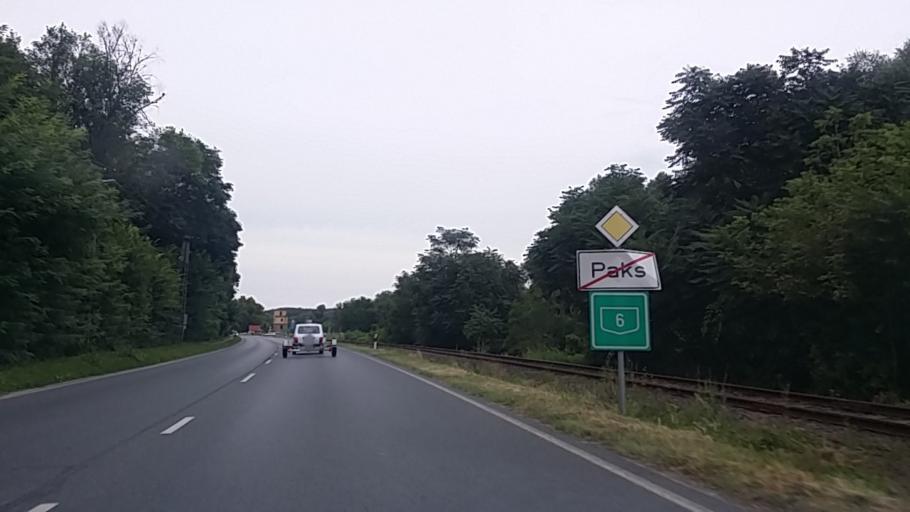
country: HU
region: Tolna
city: Paks
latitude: 46.6354
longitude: 18.8768
